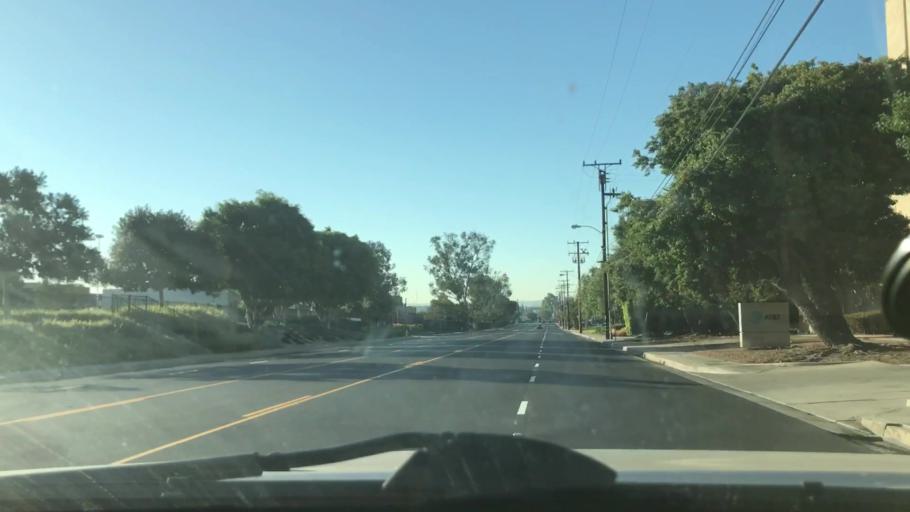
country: US
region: California
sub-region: Los Angeles County
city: Del Aire
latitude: 33.9147
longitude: -118.3832
